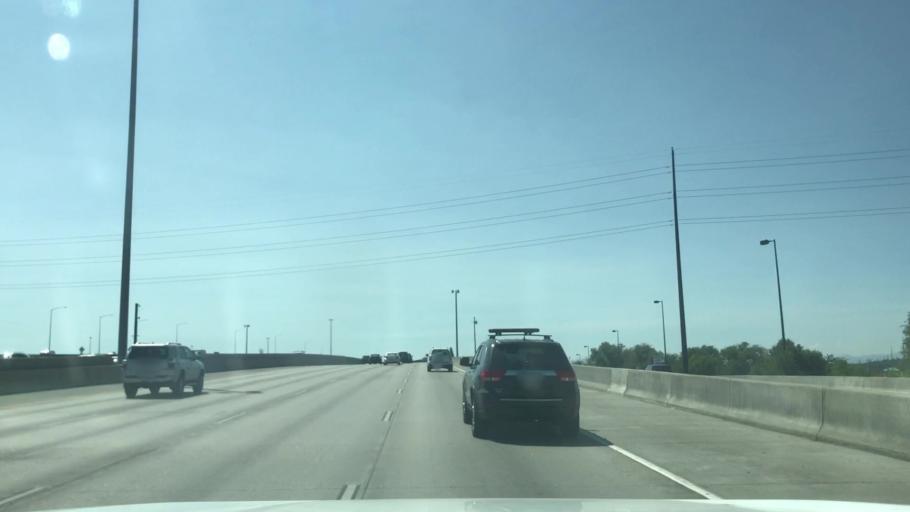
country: US
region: Colorado
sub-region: Denver County
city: Denver
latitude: 39.7089
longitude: -104.9982
